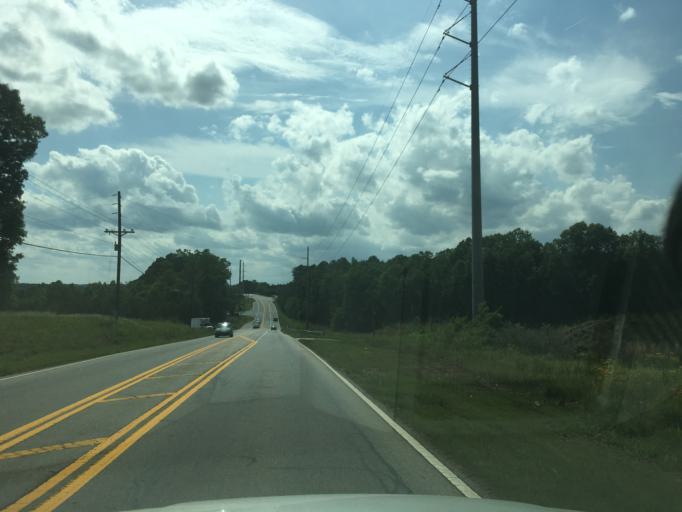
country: US
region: Georgia
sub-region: Jackson County
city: Braselton
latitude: 34.1055
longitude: -83.7756
